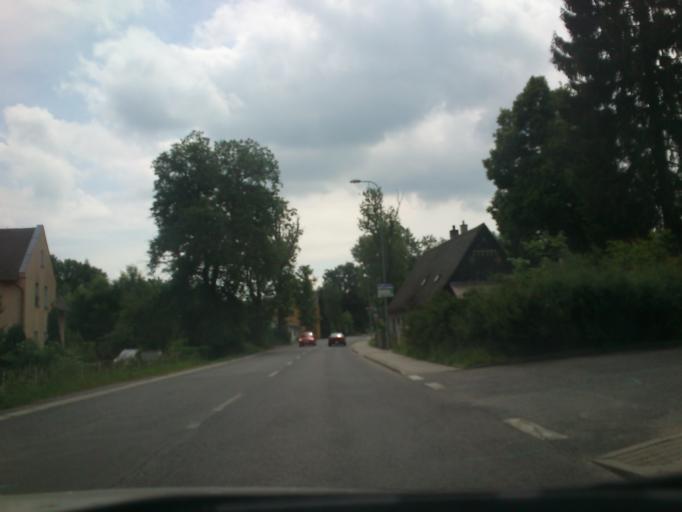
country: CZ
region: Liberecky
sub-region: Okres Liberec
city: Liberec
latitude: 50.7341
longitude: 15.0569
